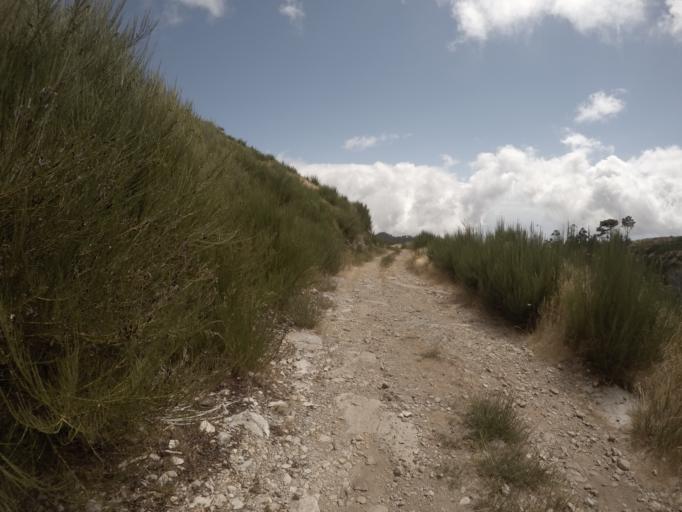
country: PT
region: Madeira
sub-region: Camara de Lobos
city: Curral das Freiras
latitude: 32.7120
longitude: -16.9902
